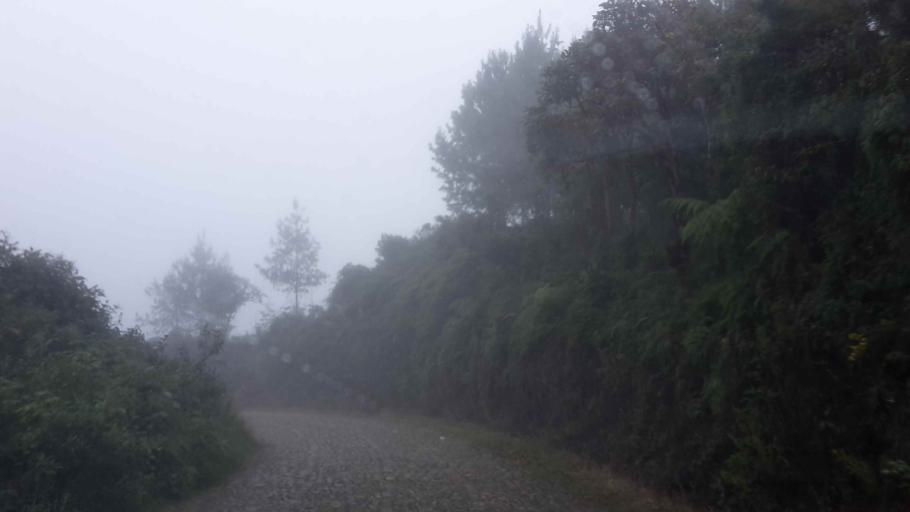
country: BO
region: Cochabamba
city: Colomi
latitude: -17.1218
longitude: -65.9628
